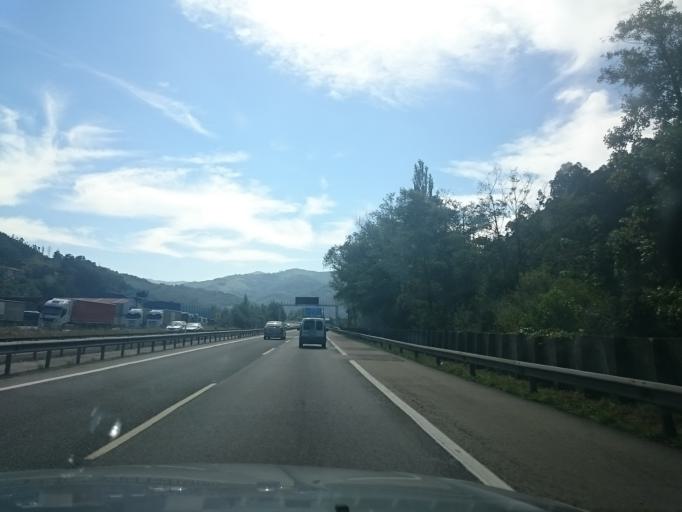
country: ES
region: Asturias
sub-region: Province of Asturias
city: Mieres
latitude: 43.2677
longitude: -5.7992
